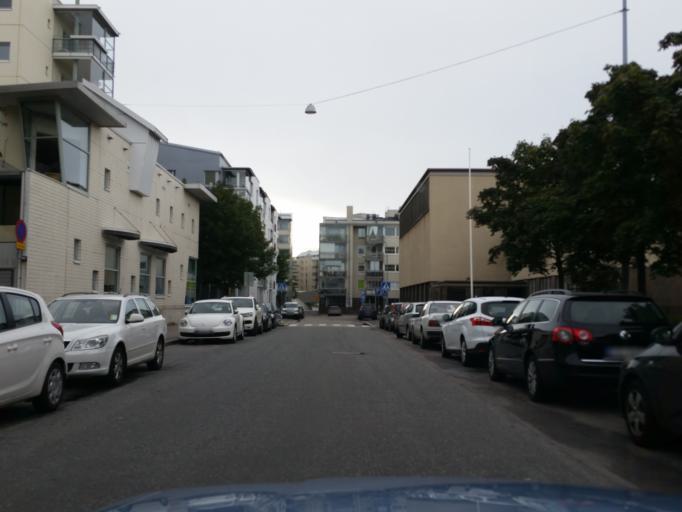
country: FI
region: Uusimaa
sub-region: Helsinki
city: Helsinki
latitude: 60.1627
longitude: 24.9181
